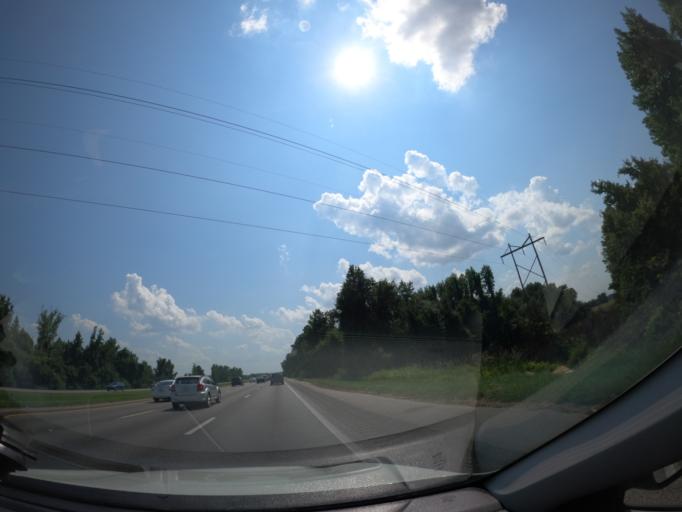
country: US
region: South Carolina
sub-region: Richland County
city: Columbia
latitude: 33.9462
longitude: -80.9999
